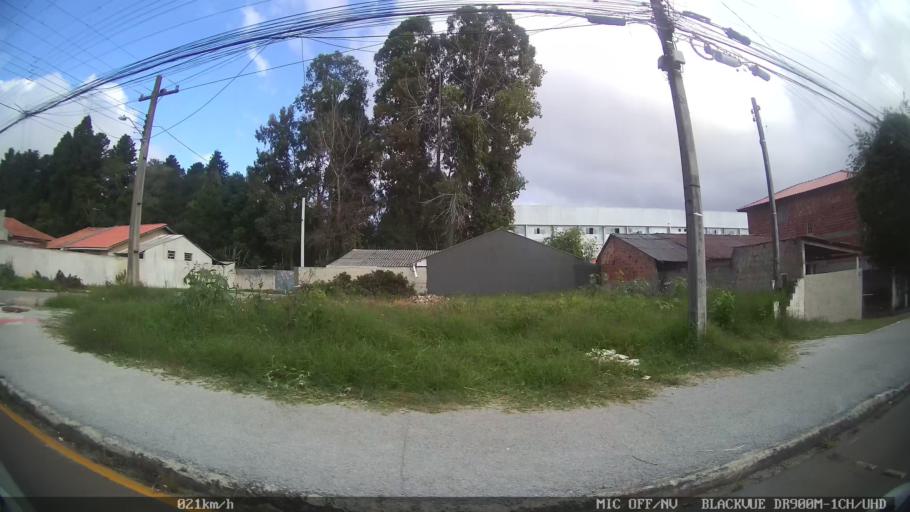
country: BR
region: Parana
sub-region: Pinhais
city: Pinhais
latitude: -25.3962
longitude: -49.1845
